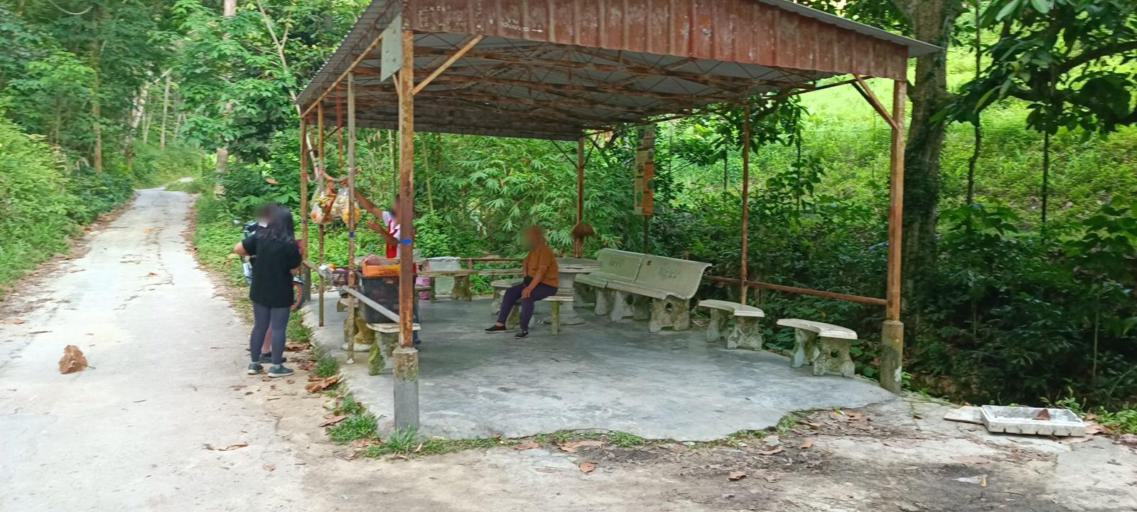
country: MY
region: Penang
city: Kampung Sungai Ara
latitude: 5.3250
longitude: 100.2480
